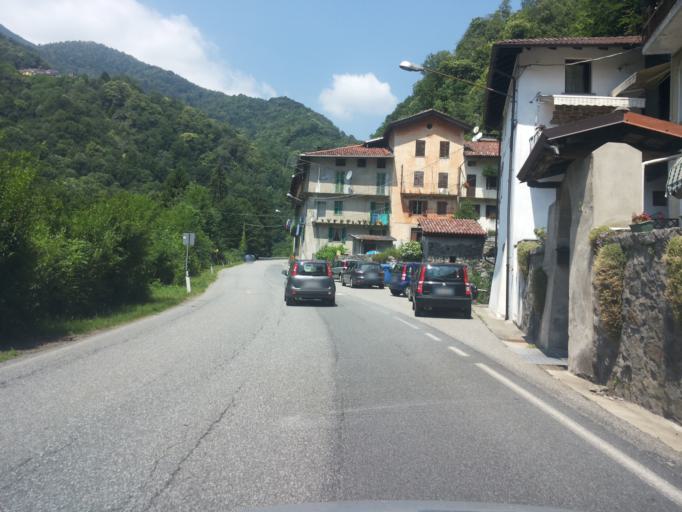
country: IT
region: Piedmont
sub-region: Provincia di Biella
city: Sagliano Micca
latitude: 45.6392
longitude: 8.0287
